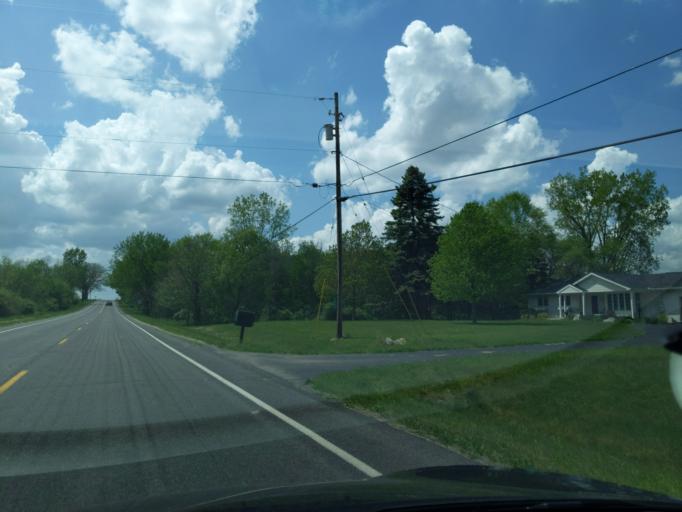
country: US
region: Michigan
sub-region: Ingham County
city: Mason
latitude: 42.5965
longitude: -84.4184
